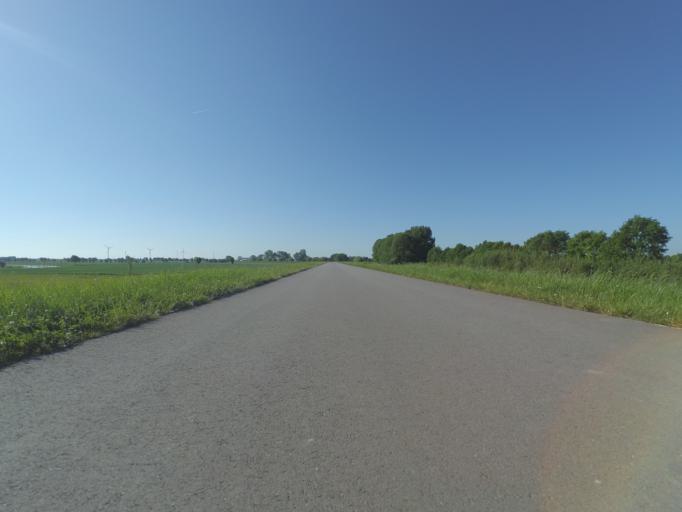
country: NL
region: Gelderland
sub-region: Gemeente Voorst
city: Voorst
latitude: 52.1782
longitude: 6.1648
